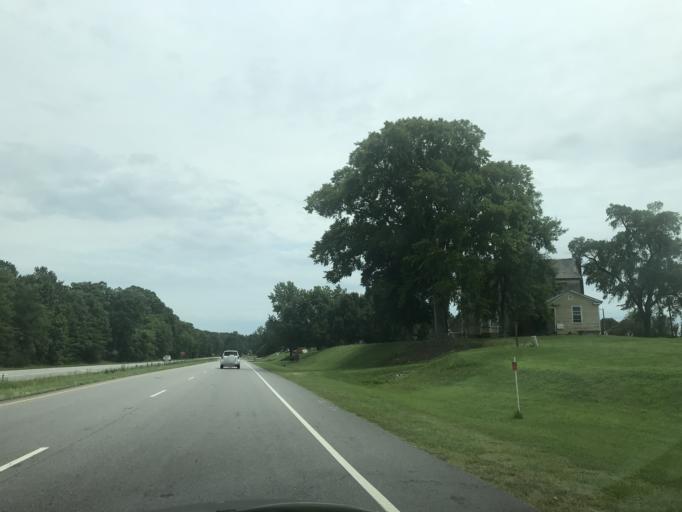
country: US
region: North Carolina
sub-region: Franklin County
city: Franklinton
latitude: 36.1874
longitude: -78.4492
